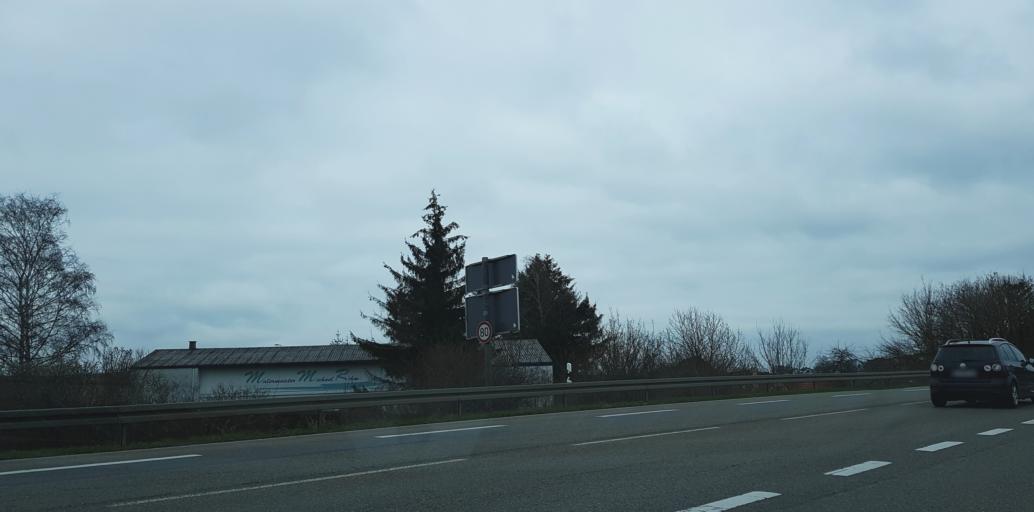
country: DE
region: Baden-Wuerttemberg
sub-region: Tuebingen Region
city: Ehingen
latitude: 48.2895
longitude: 9.7330
